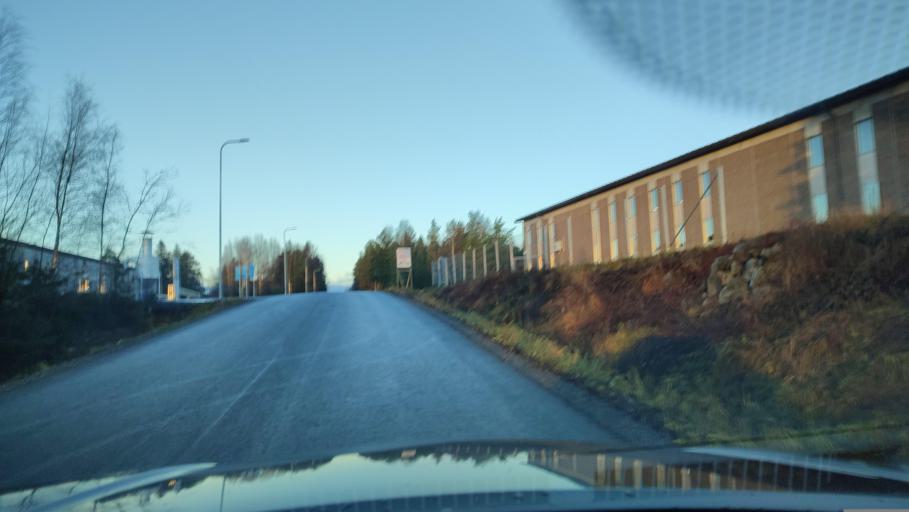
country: FI
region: Ostrobothnia
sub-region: Sydosterbotten
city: Naerpes
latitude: 62.4779
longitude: 21.3752
